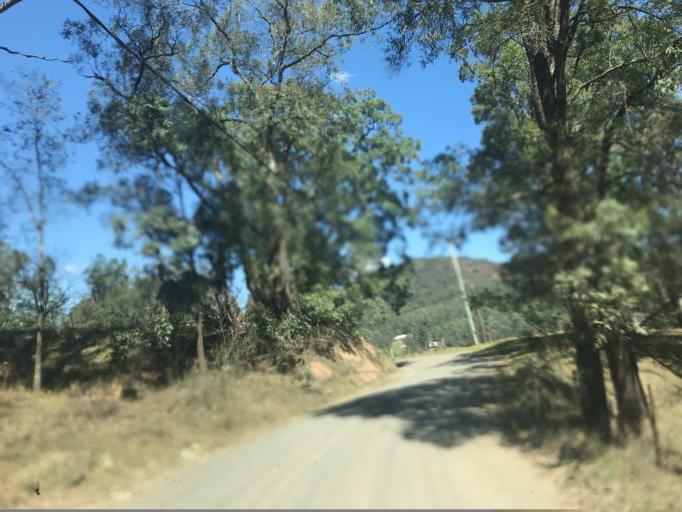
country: AU
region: New South Wales
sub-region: Hornsby Shire
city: Glenorie
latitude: -33.2797
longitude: 150.9688
